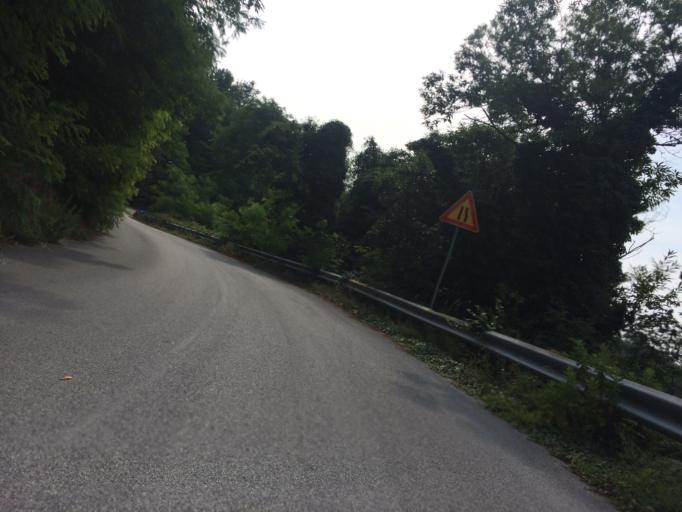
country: IT
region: Liguria
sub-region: Provincia di Savona
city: San Giovanni
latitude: 44.4018
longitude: 8.4909
